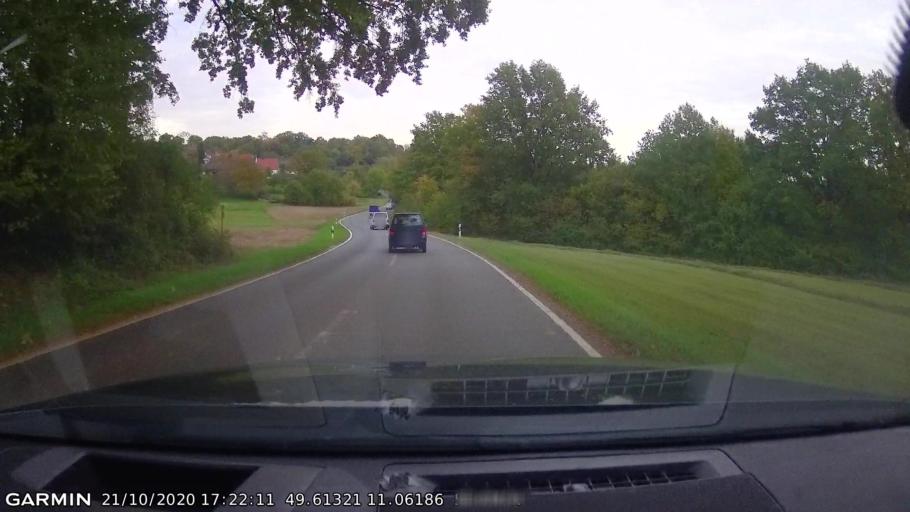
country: DE
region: Bavaria
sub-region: Regierungsbezirk Mittelfranken
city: Marloffstein
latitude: 49.6132
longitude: 11.0622
